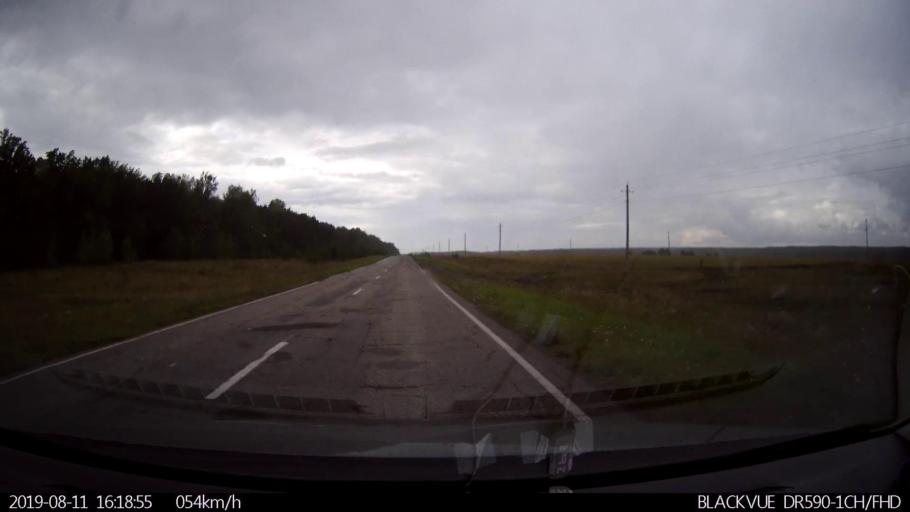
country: RU
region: Ulyanovsk
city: Mayna
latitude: 54.0600
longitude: 47.6093
